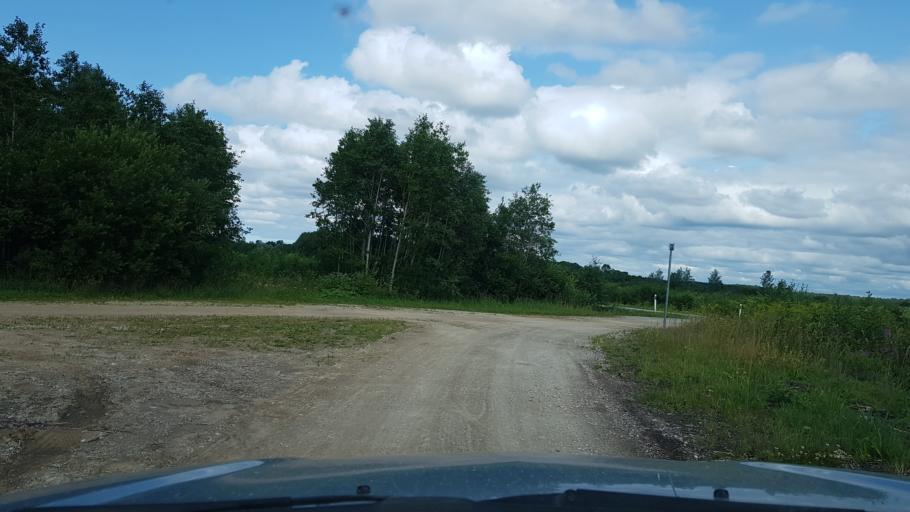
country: EE
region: Ida-Virumaa
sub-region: Narva-Joesuu linn
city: Narva-Joesuu
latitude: 59.3693
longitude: 27.9278
